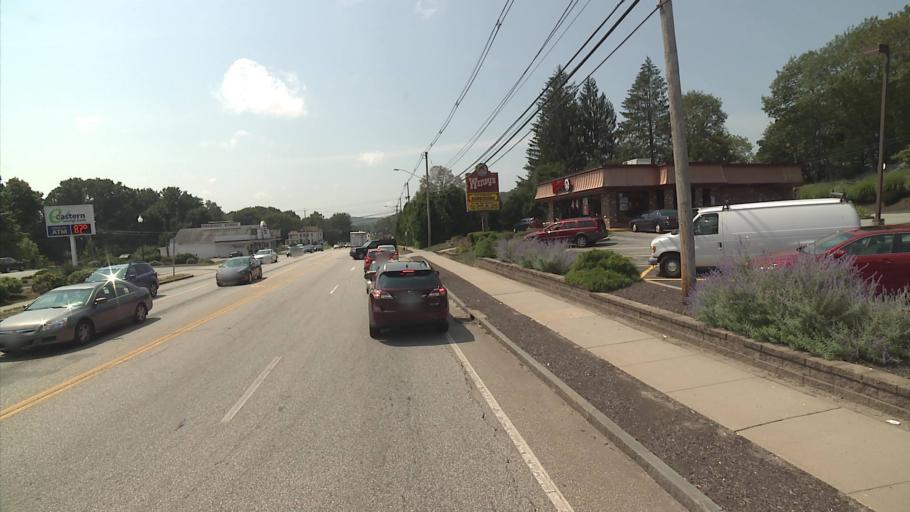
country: US
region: Connecticut
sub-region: New London County
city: Norwich
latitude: 41.5154
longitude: -72.1027
